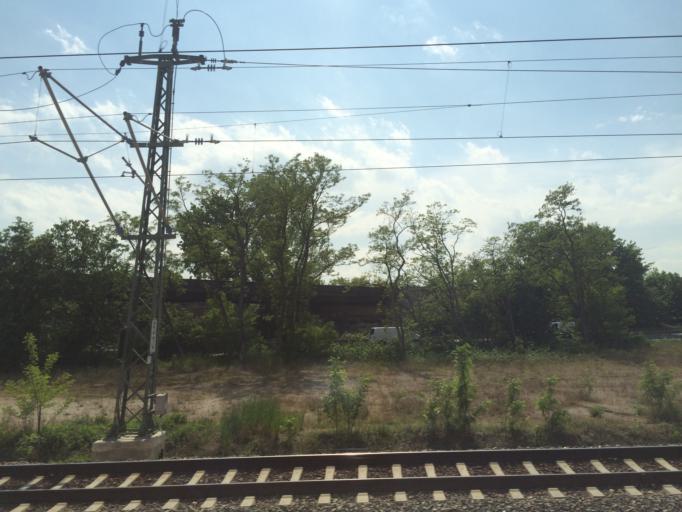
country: DE
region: Bavaria
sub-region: Regierungsbezirk Mittelfranken
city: Wetzendorf
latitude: 49.4587
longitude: 11.0216
